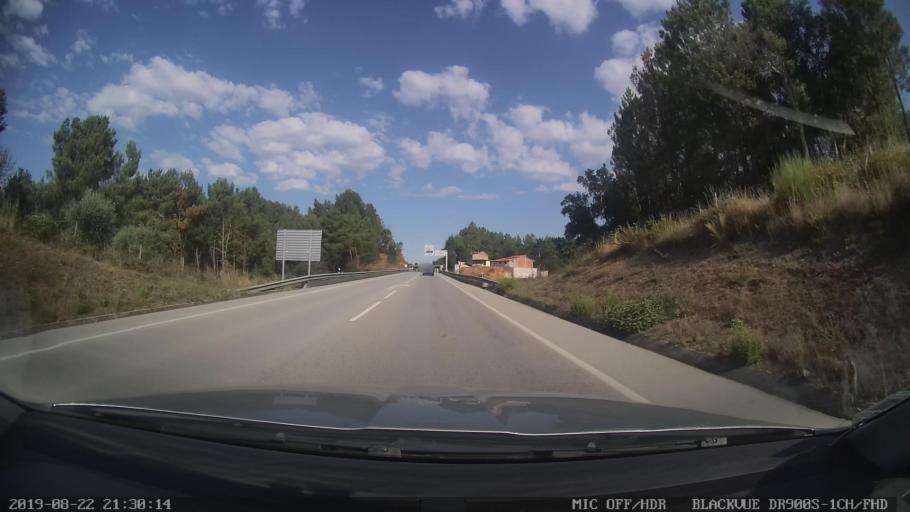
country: PT
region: Leiria
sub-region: Pedrogao Grande
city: Pedrogao Grande
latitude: 39.9083
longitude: -8.1480
